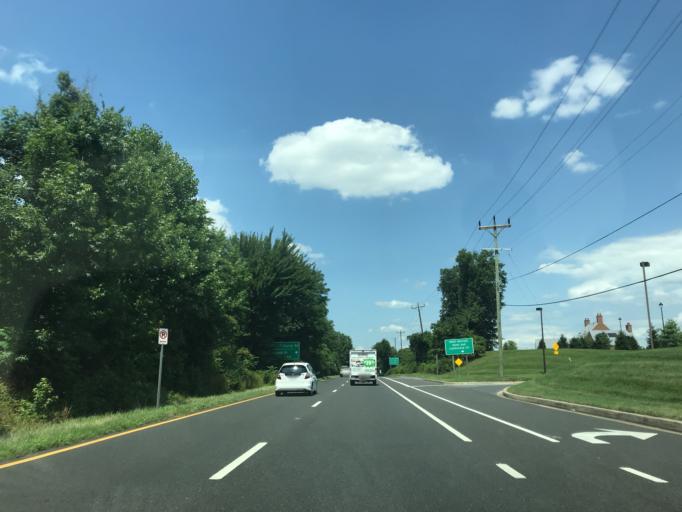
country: US
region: Maryland
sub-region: Prince George's County
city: College Park
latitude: 38.9875
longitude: -76.9549
